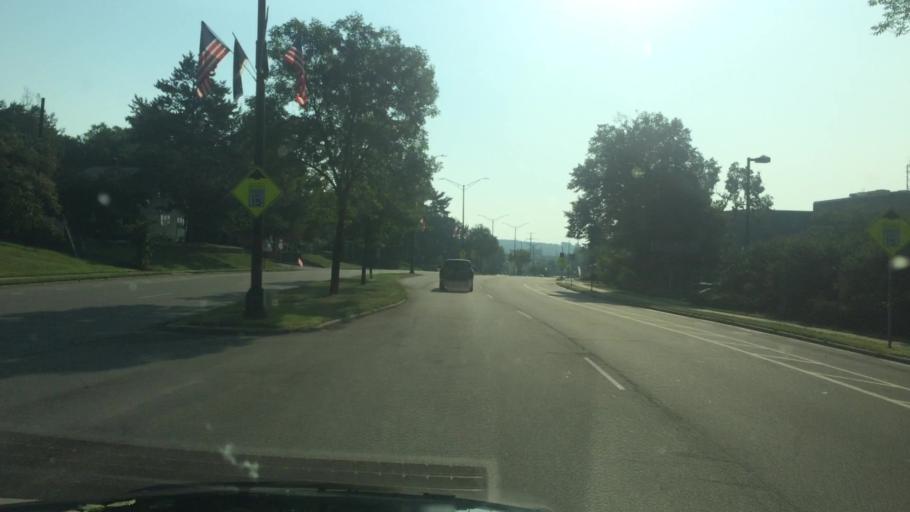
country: US
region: Wisconsin
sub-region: Marathon County
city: Wausau
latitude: 44.9591
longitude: -89.6454
